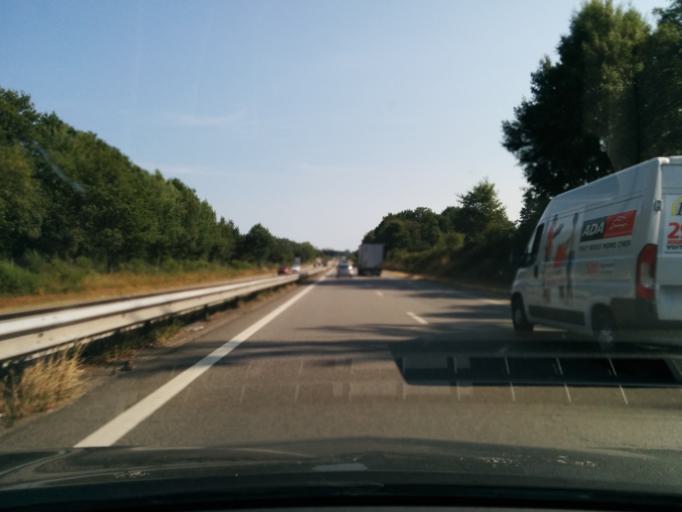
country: FR
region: Limousin
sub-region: Departement de la Haute-Vienne
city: Rilhac-Rancon
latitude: 45.9023
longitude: 1.2919
